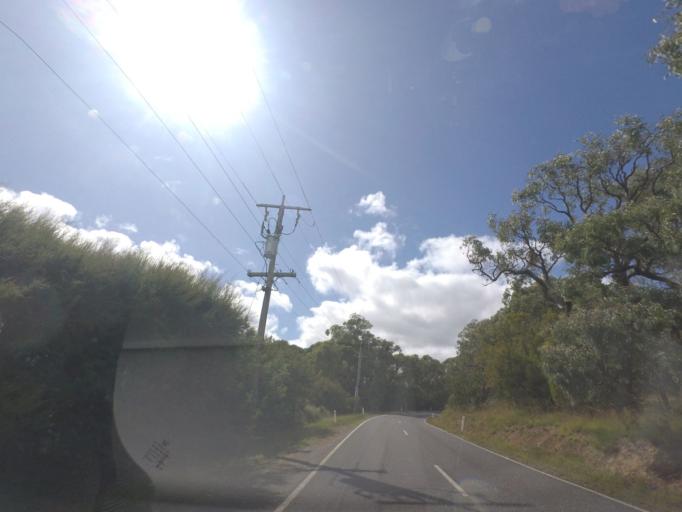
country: AU
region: Victoria
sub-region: Yarra Ranges
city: Launching Place
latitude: -37.7895
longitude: 145.5705
